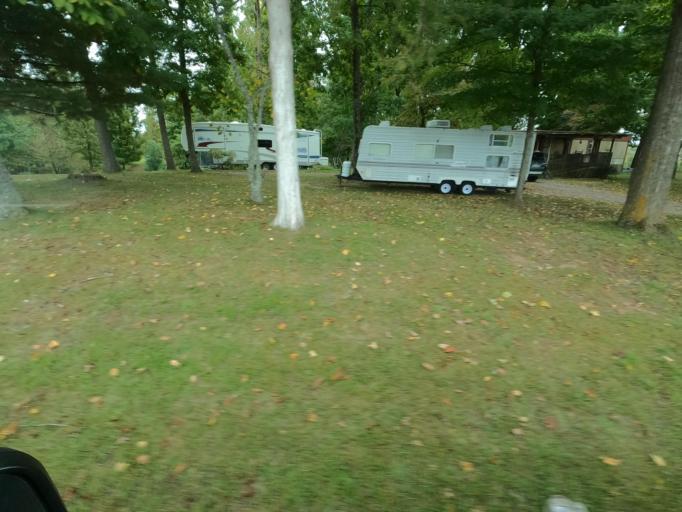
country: US
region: Tennessee
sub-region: Washington County
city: Jonesborough
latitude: 36.2377
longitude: -82.5842
